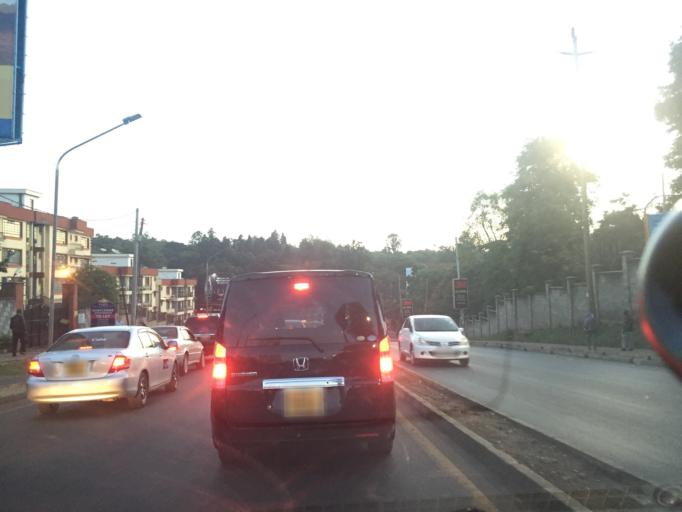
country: KE
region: Nairobi Area
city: Nairobi
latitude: -1.2724
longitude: 36.8012
